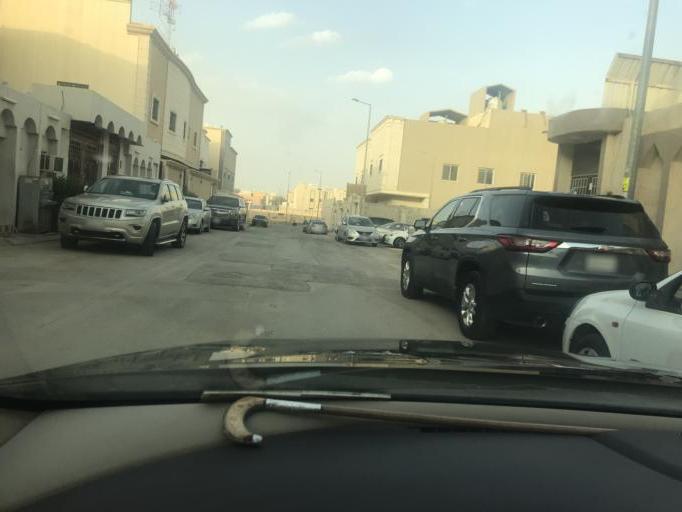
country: SA
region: Ar Riyad
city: Riyadh
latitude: 24.7365
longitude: 46.7775
